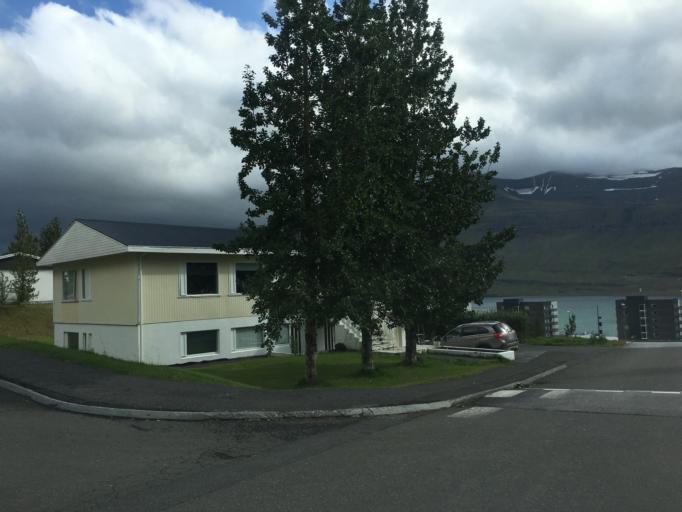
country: IS
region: East
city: Reydarfjoerdur
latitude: 65.0358
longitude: -14.2097
